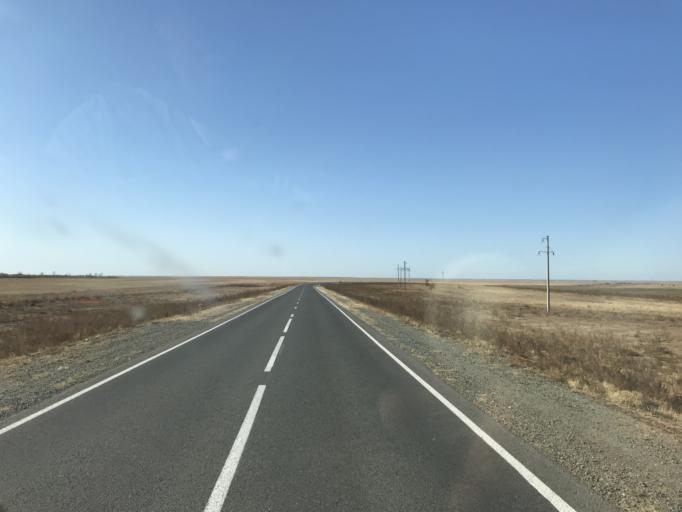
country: KZ
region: Pavlodar
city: Kurchatov
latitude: 50.9614
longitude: 79.3331
